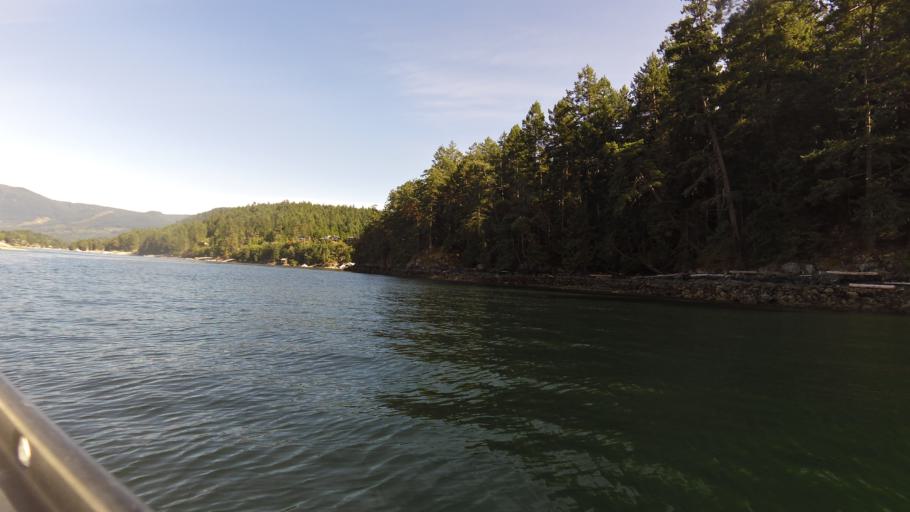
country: CA
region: British Columbia
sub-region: Sunshine Coast Regional District
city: Sechelt
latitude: 49.6272
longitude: -124.0576
